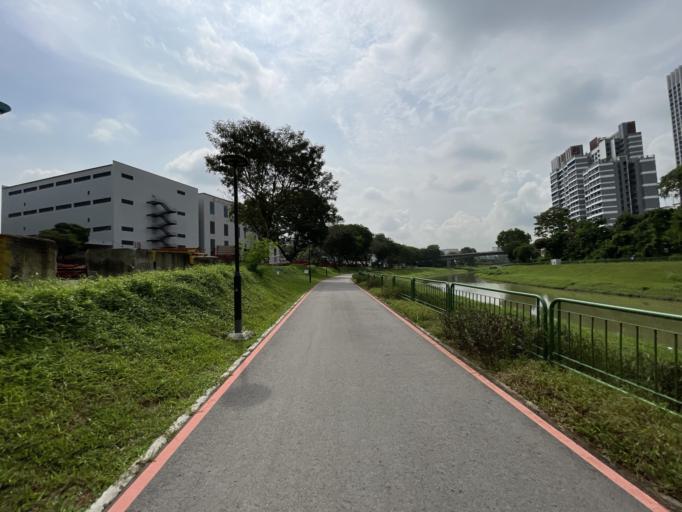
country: SG
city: Singapore
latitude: 1.3244
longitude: 103.7615
